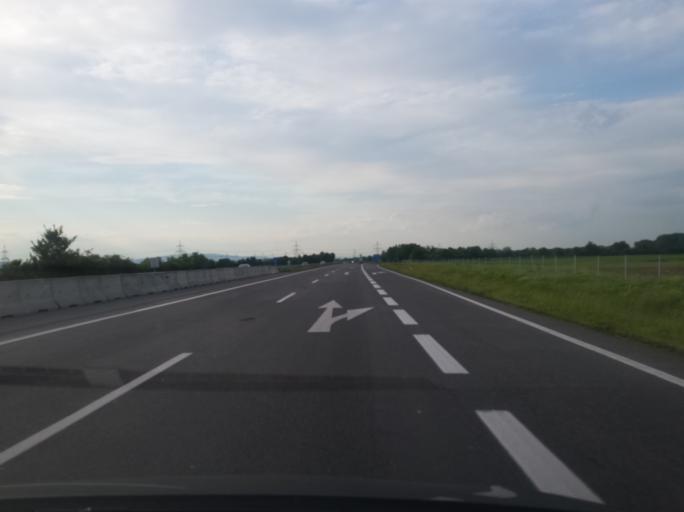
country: AT
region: Burgenland
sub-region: Eisenstadt-Umgebung
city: Steinbrunn
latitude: 47.8623
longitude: 16.4210
